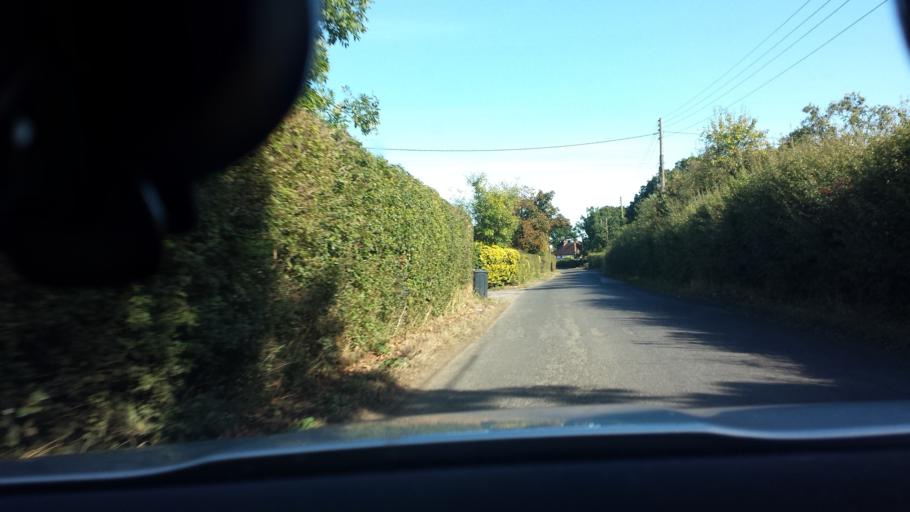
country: GB
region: England
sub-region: Kent
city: Staplehurst
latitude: 51.1941
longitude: 0.5517
